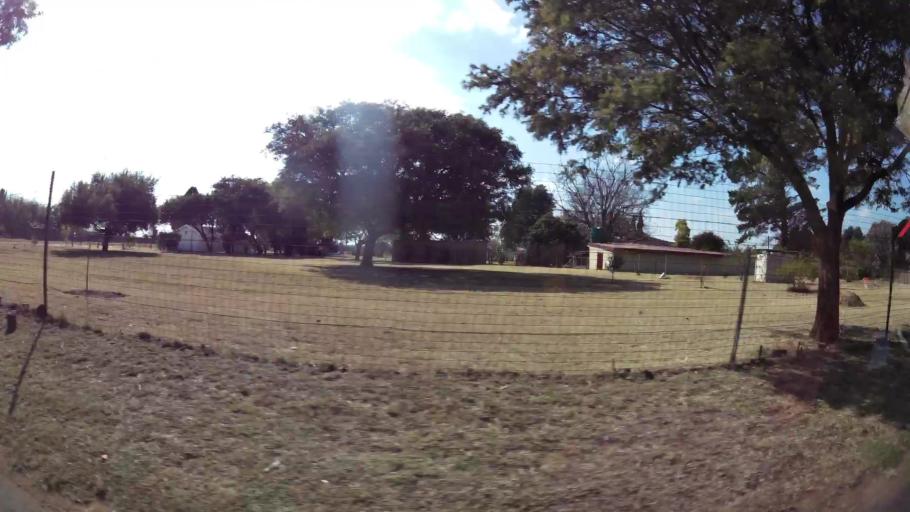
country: ZA
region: Gauteng
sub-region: Ekurhuleni Metropolitan Municipality
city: Benoni
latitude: -26.0942
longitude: 28.3332
